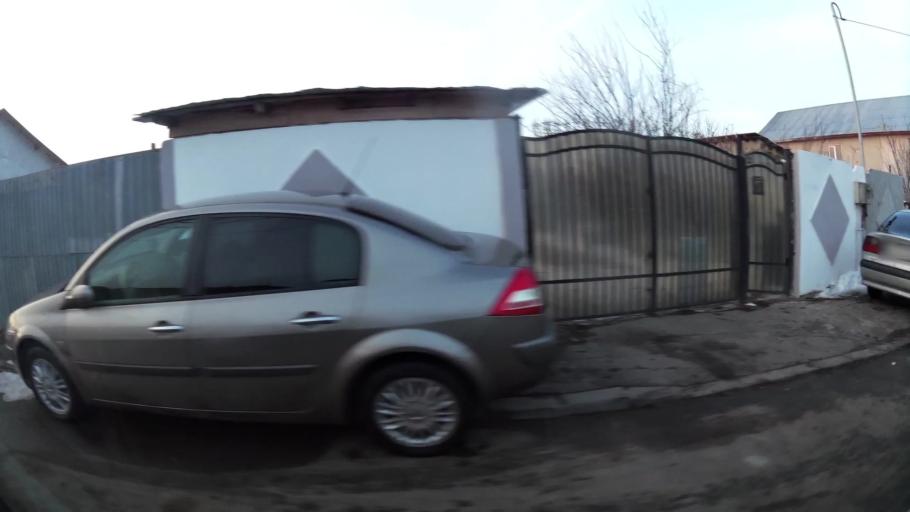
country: RO
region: Ilfov
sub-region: Comuna Magurele
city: Magurele
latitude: 44.3888
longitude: 26.0330
